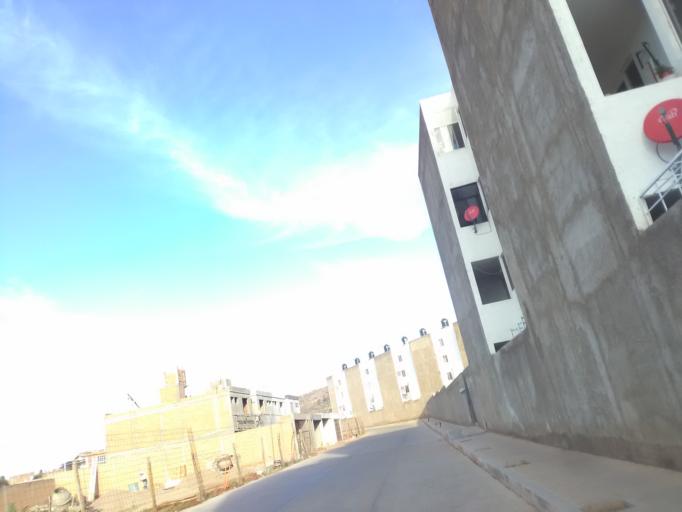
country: MX
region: Durango
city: Victoria de Durango
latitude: 24.0550
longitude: -104.6522
